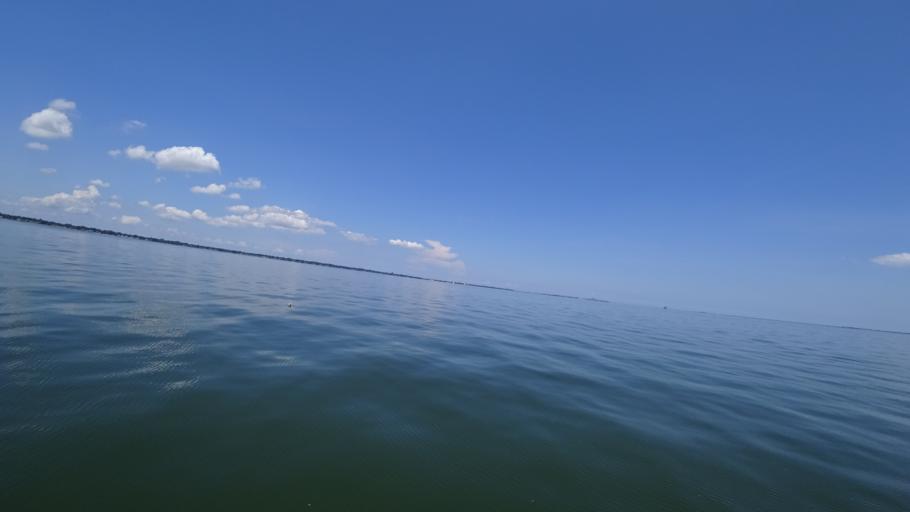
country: US
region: Virginia
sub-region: City of Newport News
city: Newport News
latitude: 36.9679
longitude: -76.3756
